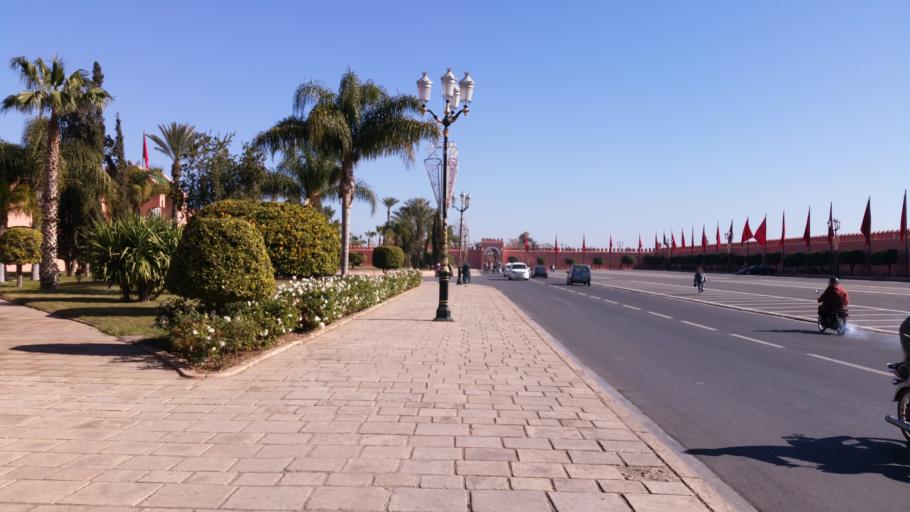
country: MA
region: Marrakech-Tensift-Al Haouz
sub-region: Marrakech
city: Marrakesh
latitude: 31.6127
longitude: -7.9838
